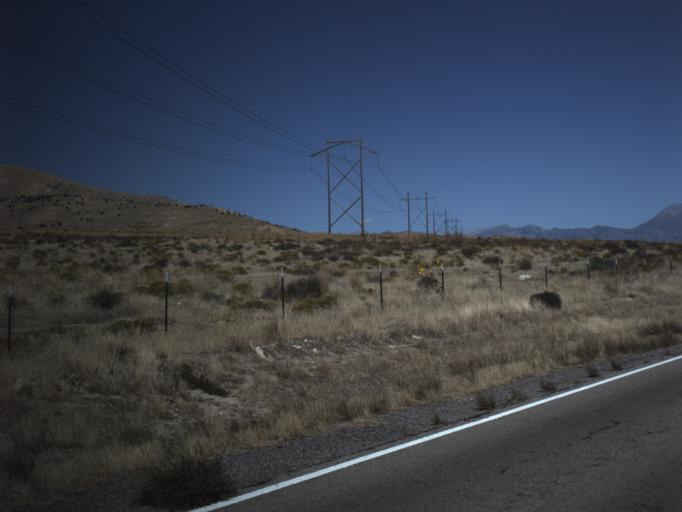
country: US
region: Utah
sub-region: Utah County
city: Eagle Mountain
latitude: 40.1808
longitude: -111.9168
